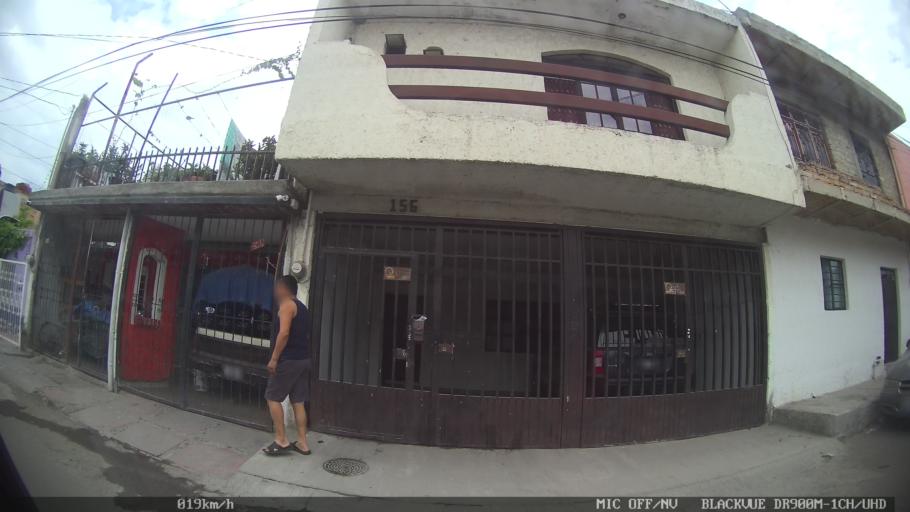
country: MX
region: Jalisco
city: Tlaquepaque
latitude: 20.6539
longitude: -103.2630
